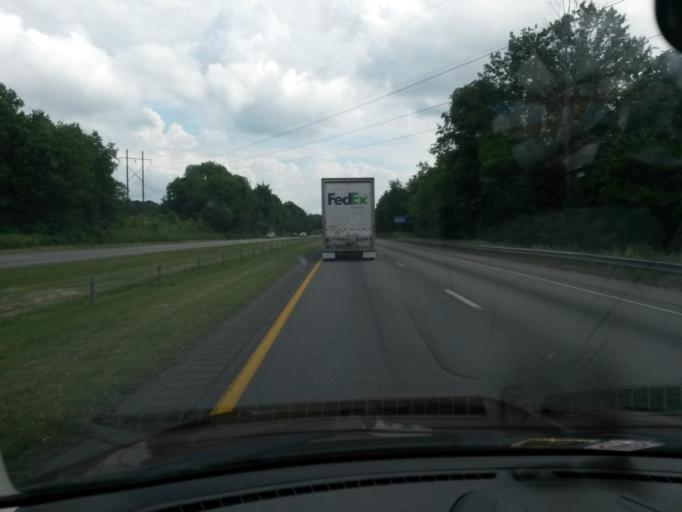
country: US
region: North Carolina
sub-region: Yadkin County
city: Jonesville
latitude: 36.2081
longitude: -80.8108
